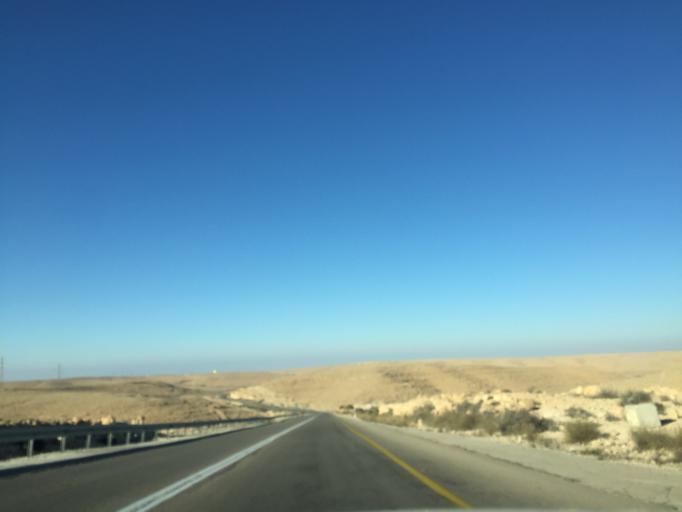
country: IL
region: Southern District
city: Mitzpe Ramon
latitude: 30.6922
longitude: 34.7850
